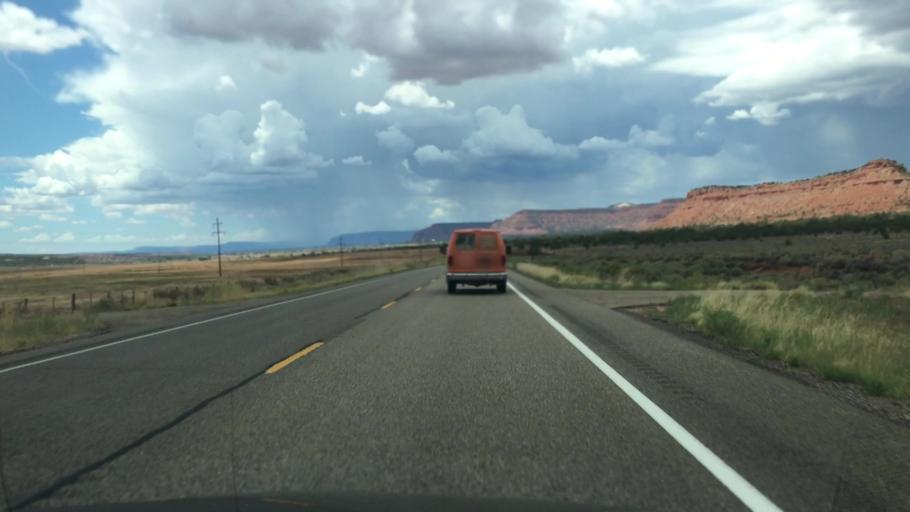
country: US
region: Utah
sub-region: Kane County
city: Kanab
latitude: 37.0386
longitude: -112.3217
